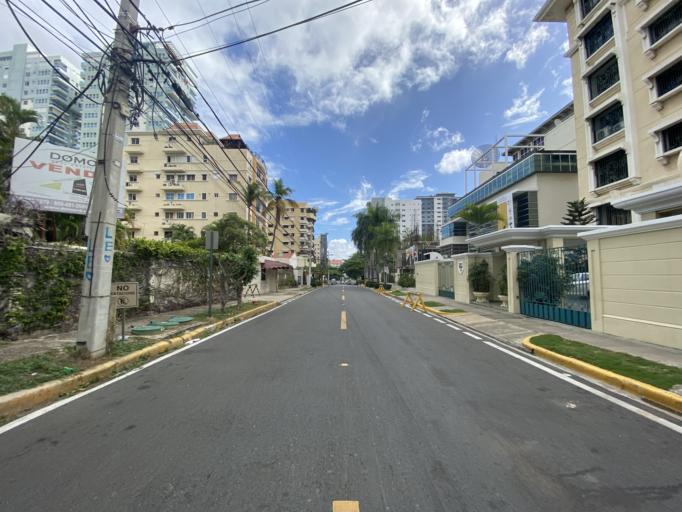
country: DO
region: Nacional
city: La Julia
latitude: 18.4694
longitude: -69.9168
